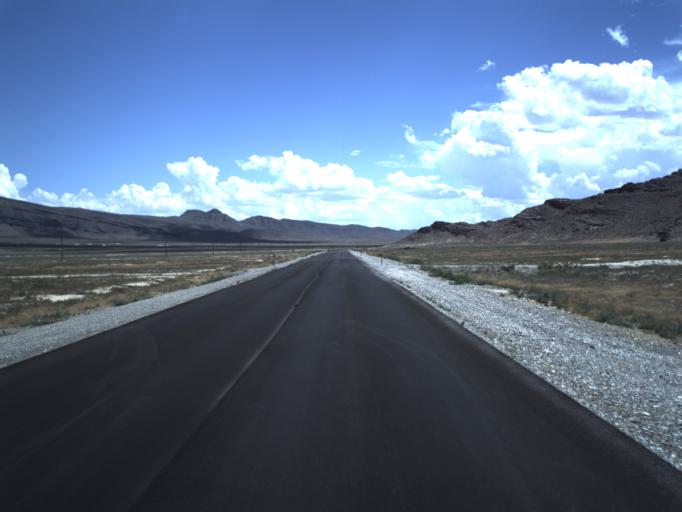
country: US
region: Utah
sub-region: Beaver County
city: Milford
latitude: 39.0693
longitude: -113.4586
